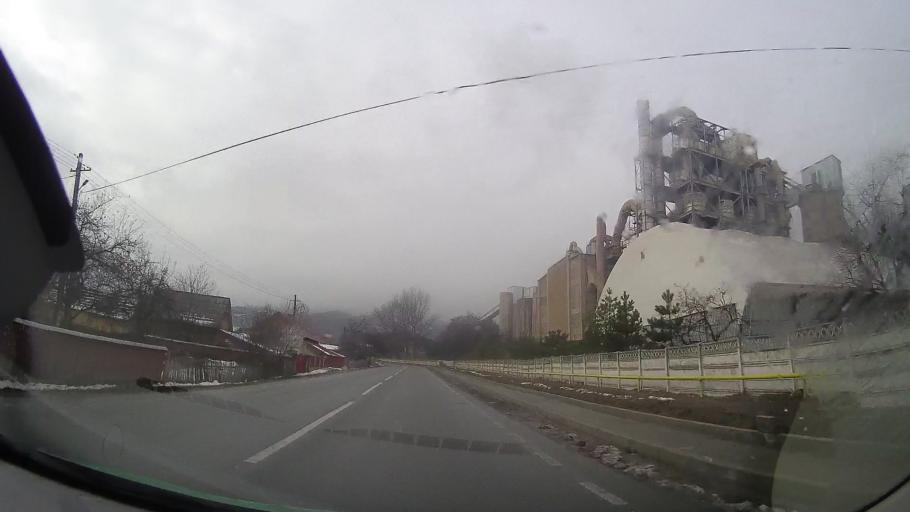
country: RO
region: Neamt
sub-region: Comuna Tasca
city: Tasca
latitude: 46.8962
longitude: 26.0304
